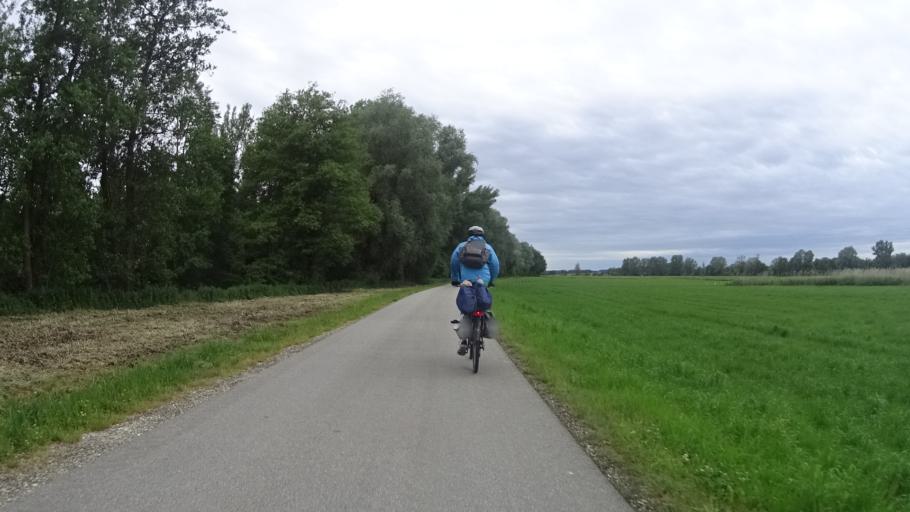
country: DE
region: Bavaria
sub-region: Lower Bavaria
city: Velden
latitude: 48.3834
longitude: 12.2803
